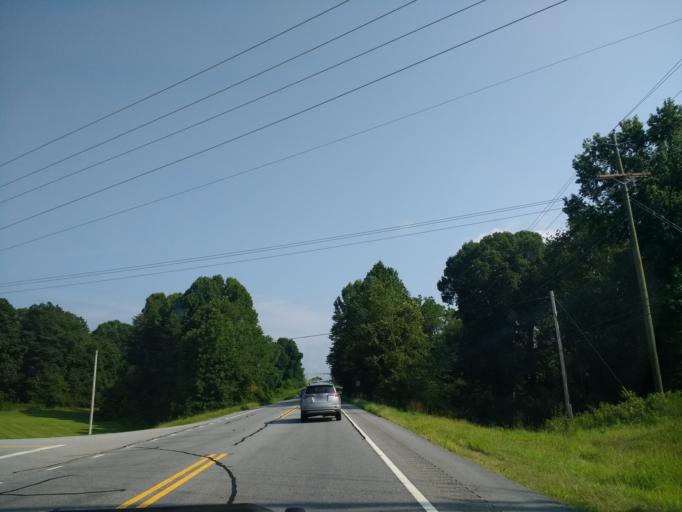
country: US
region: Georgia
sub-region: White County
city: Cleveland
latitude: 34.5373
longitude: -83.7581
